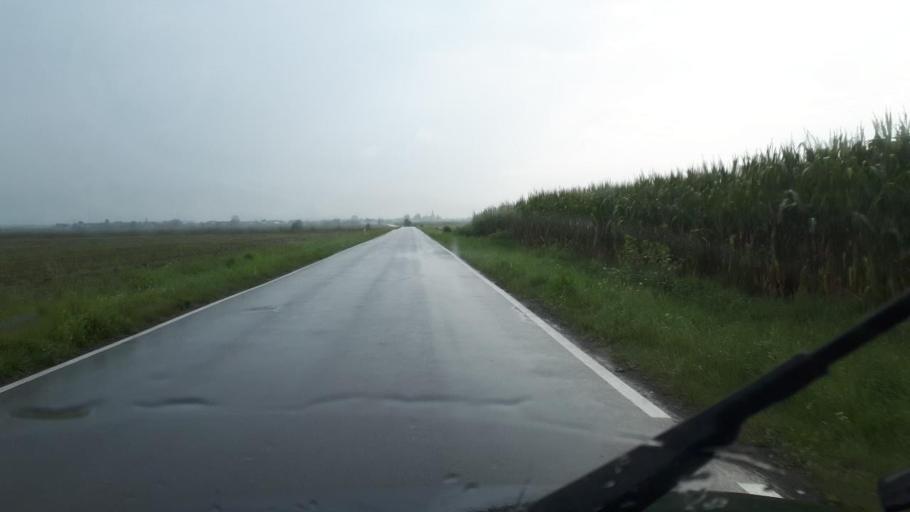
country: PL
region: Silesian Voivodeship
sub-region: Powiat gliwicki
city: Wielowies
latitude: 50.5218
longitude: 18.6338
